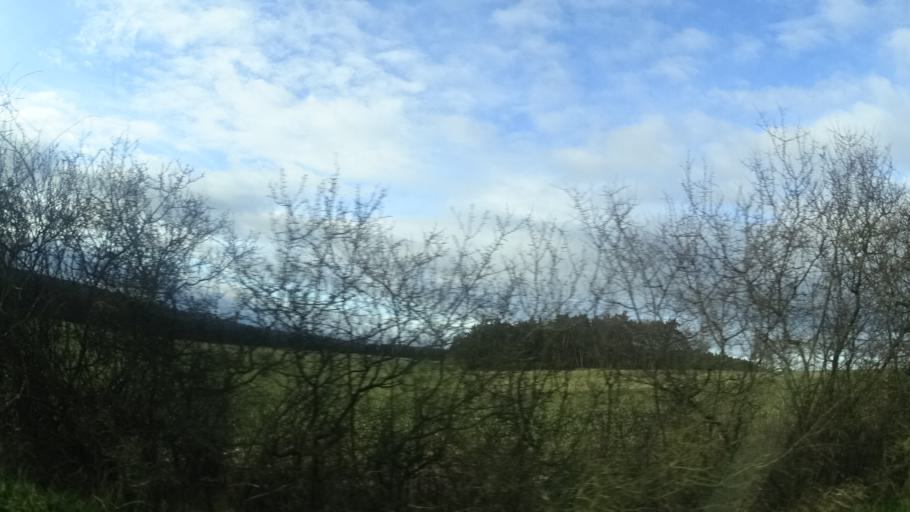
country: DE
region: Thuringia
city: Rottenbach
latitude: 50.7342
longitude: 11.1877
